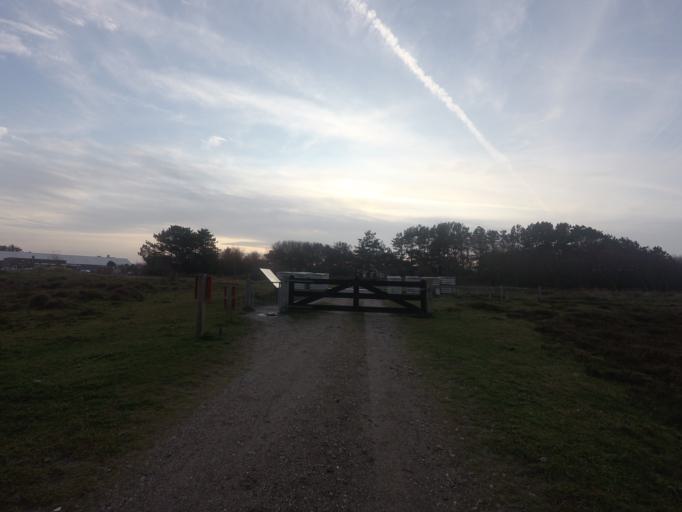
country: NL
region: North Holland
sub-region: Gemeente Texel
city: Den Burg
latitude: 53.1047
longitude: 4.7733
